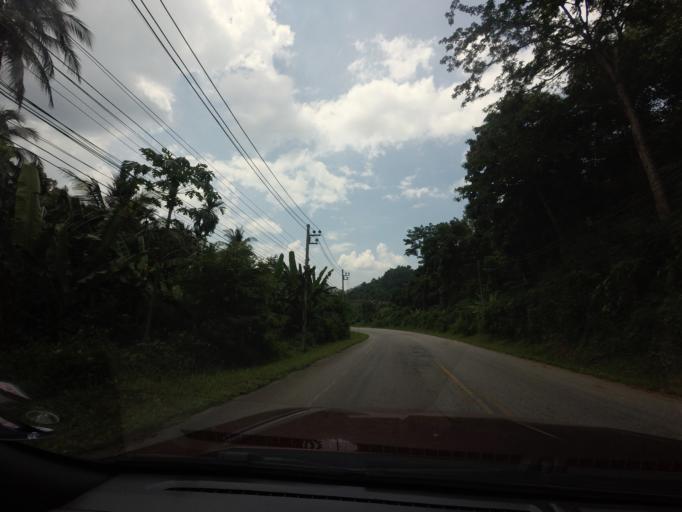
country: TH
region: Yala
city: Than To
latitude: 6.0665
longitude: 101.1975
